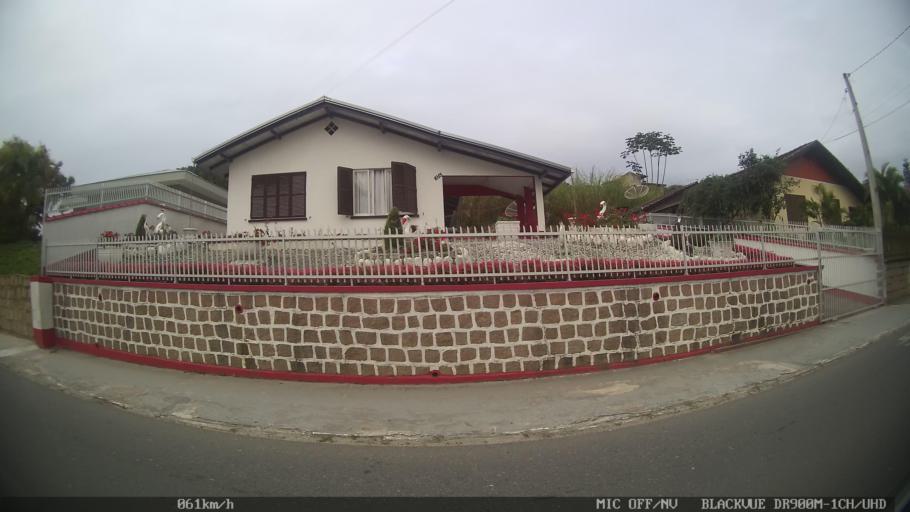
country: BR
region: Santa Catarina
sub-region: Joinville
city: Joinville
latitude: -26.2825
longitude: -48.8747
